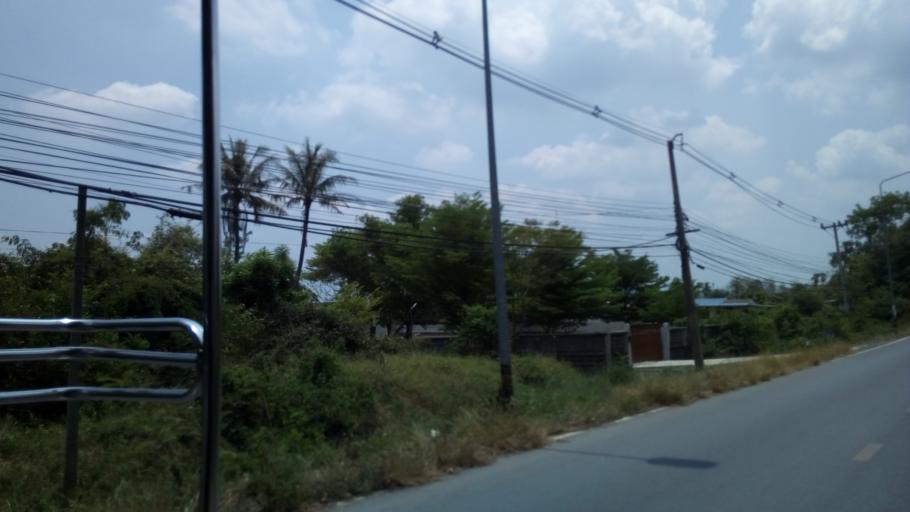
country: TH
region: Pathum Thani
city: Sam Khok
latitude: 14.0847
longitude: 100.5226
